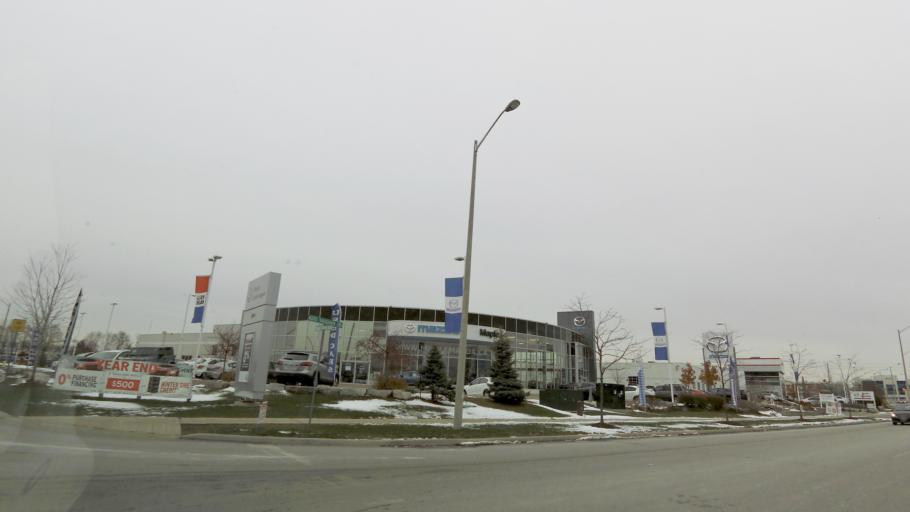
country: CA
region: Ontario
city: Vaughan
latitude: 43.8357
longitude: -79.5369
